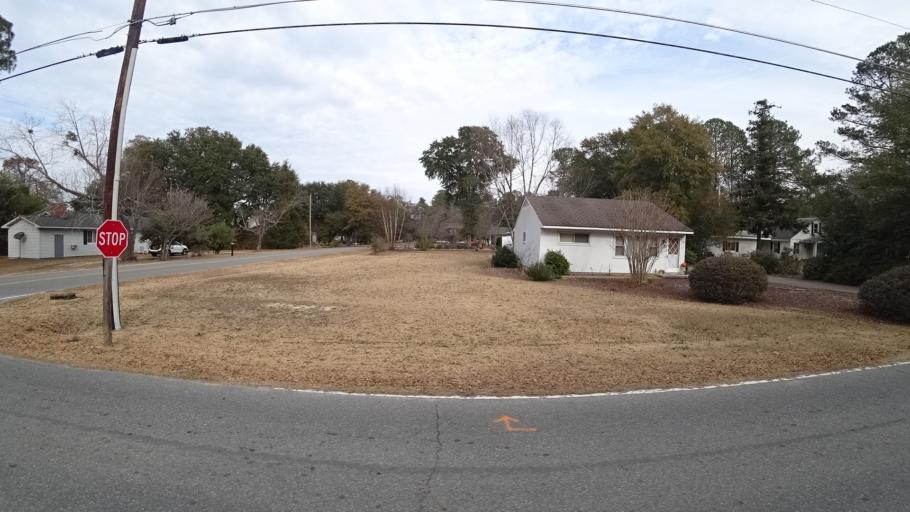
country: US
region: North Carolina
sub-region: Moore County
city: Pinehurst
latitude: 35.2016
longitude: -79.4663
